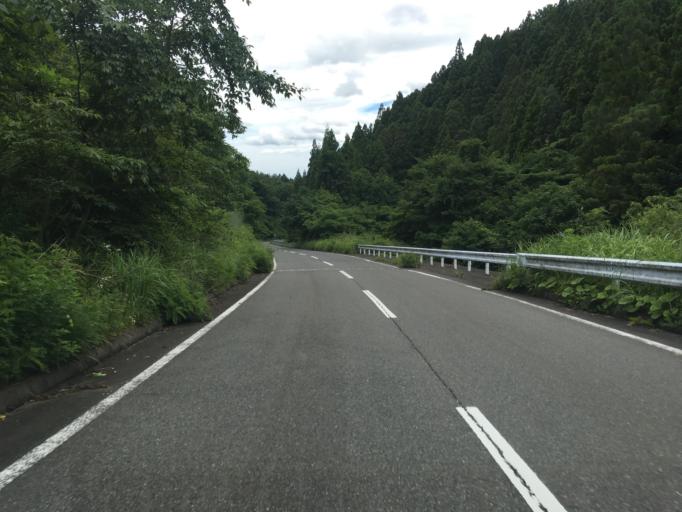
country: JP
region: Miyagi
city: Marumori
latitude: 37.7017
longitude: 140.8787
